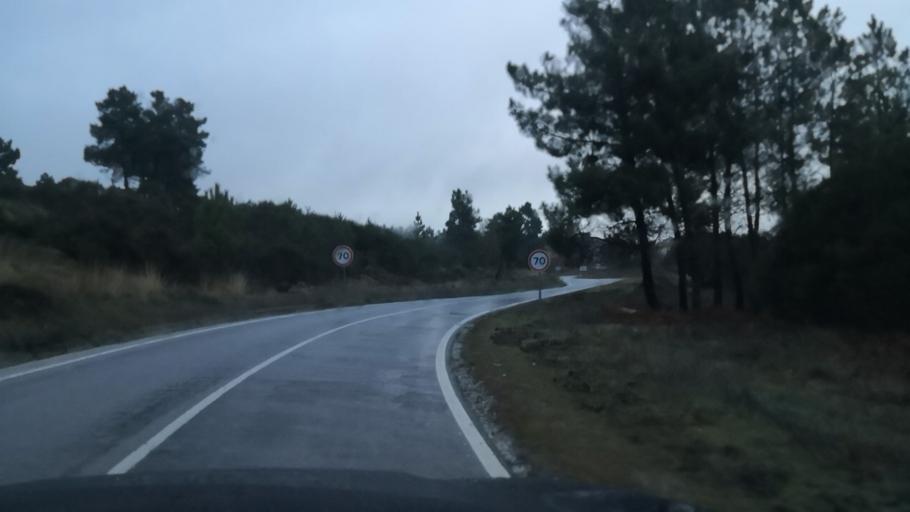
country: PT
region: Vila Real
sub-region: Murca
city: Murca
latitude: 41.4184
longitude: -7.5065
